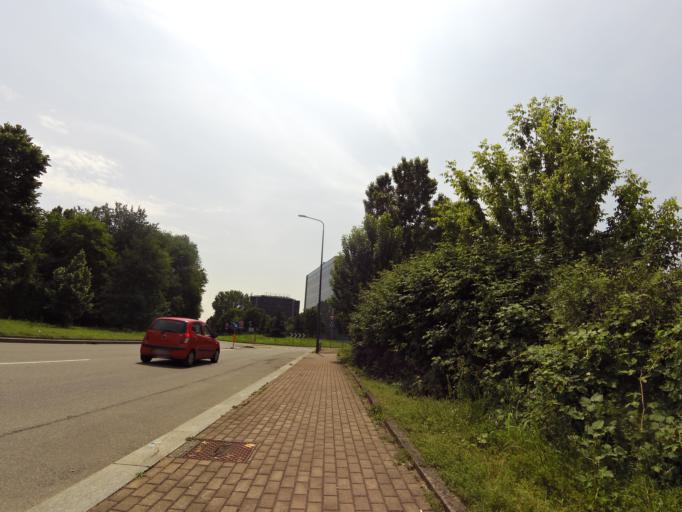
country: IT
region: Lombardy
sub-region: Citta metropolitana di Milano
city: Linate
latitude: 45.4356
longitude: 9.2662
